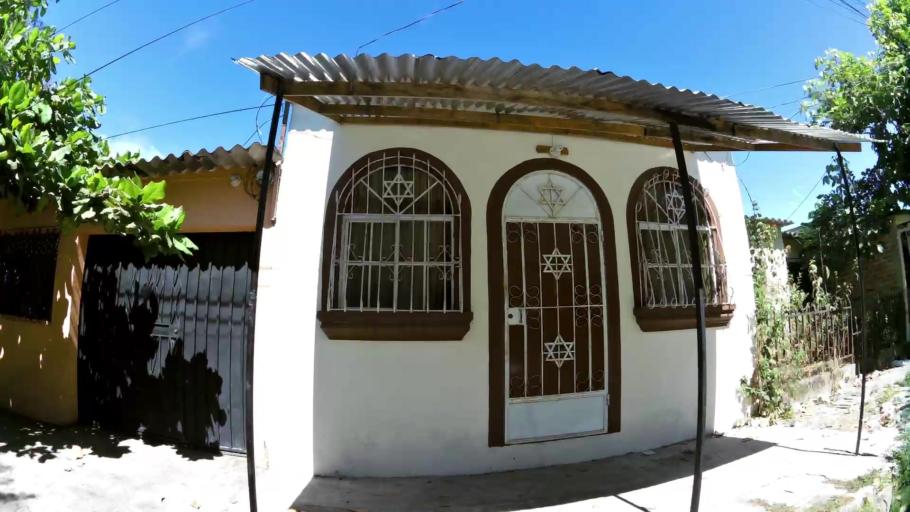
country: SV
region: San Salvador
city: Apopa
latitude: 13.8047
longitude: -89.1821
